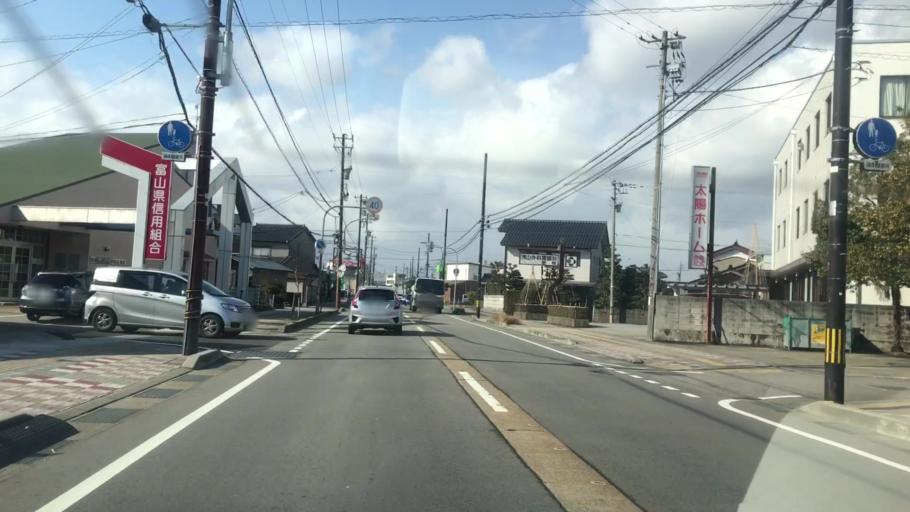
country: JP
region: Toyama
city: Takaoka
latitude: 36.7303
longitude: 137.0560
